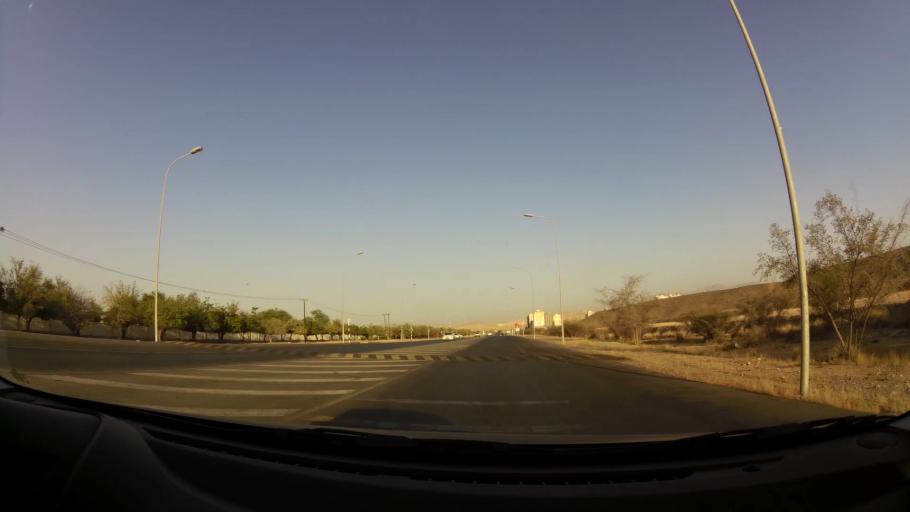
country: OM
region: Muhafazat Masqat
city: As Sib al Jadidah
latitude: 23.5813
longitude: 58.1737
